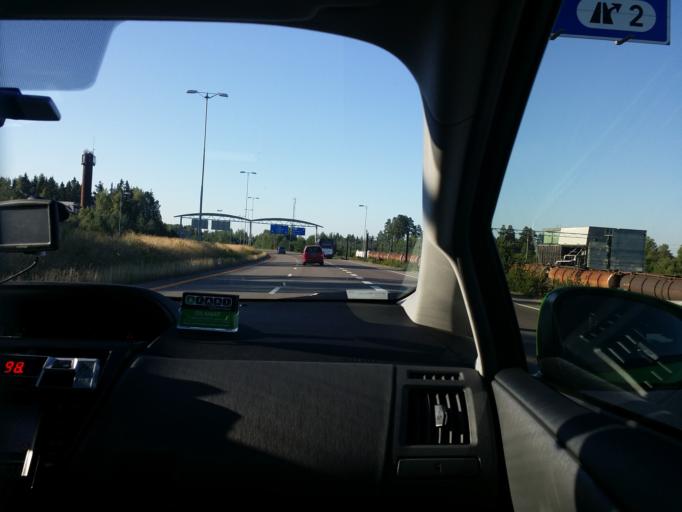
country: NO
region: Akershus
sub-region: Nannestad
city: Teigebyen
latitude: 60.1828
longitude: 11.0926
